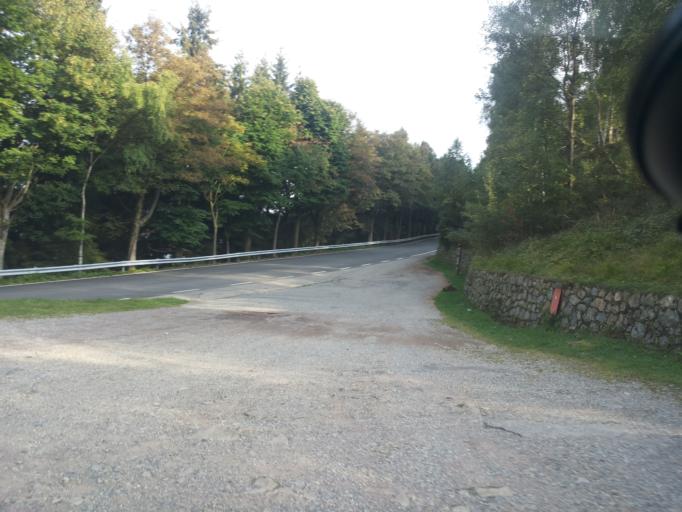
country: IT
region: Piedmont
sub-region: Provincia di Biella
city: Portula
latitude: 45.6818
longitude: 8.1424
